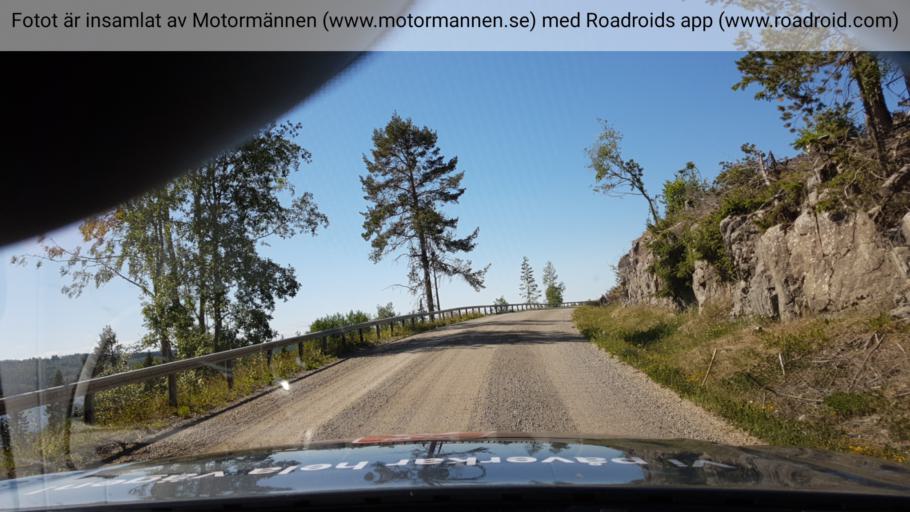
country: SE
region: Jaemtland
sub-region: OEstersunds Kommun
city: Brunflo
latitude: 62.9558
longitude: 14.9092
